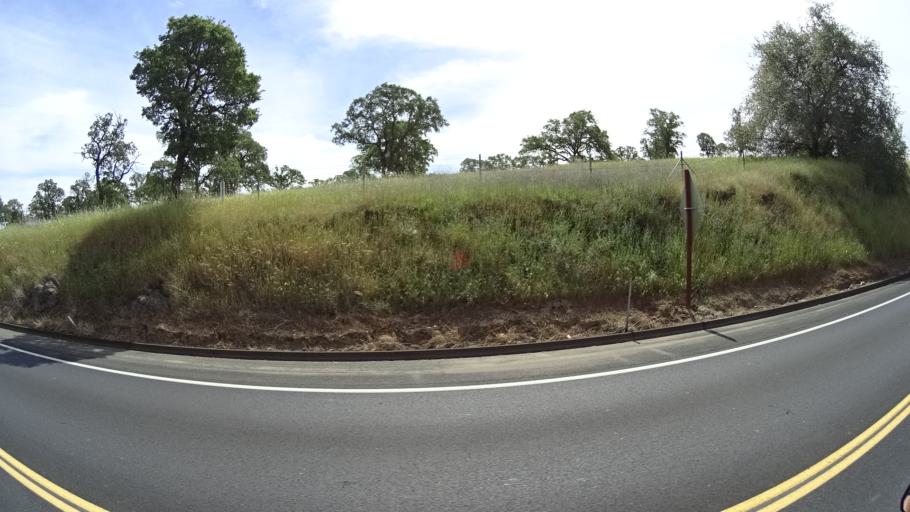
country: US
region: California
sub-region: Placer County
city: Loomis
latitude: 38.8548
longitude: -121.2192
